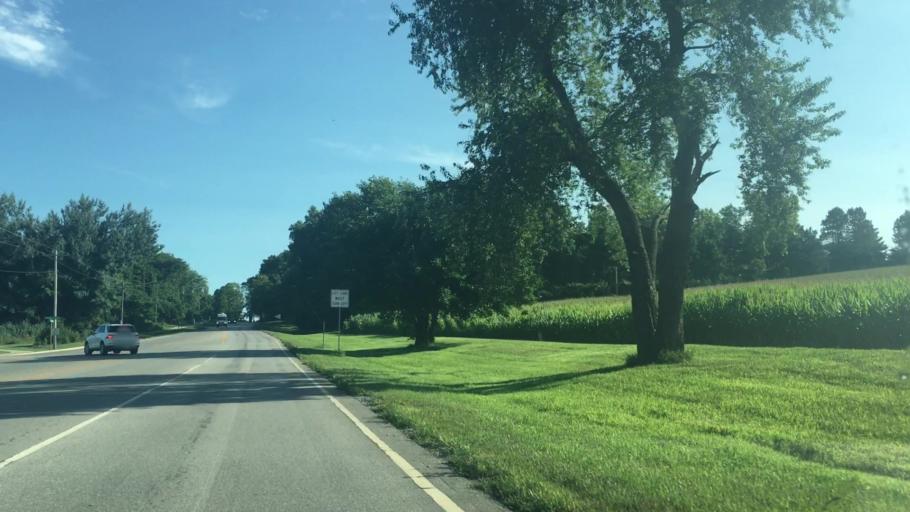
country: US
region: Iowa
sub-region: Johnson County
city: Iowa City
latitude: 41.6985
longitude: -91.5461
